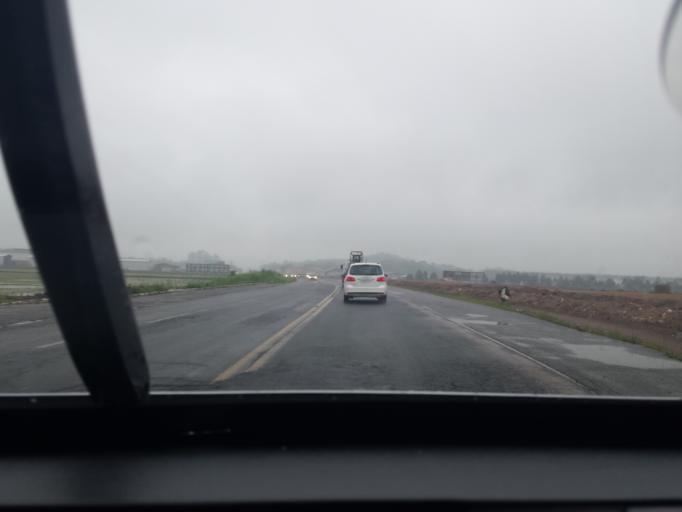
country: BR
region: Santa Catarina
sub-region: Navegantes
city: Navegantes
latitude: -26.8332
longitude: -48.7263
